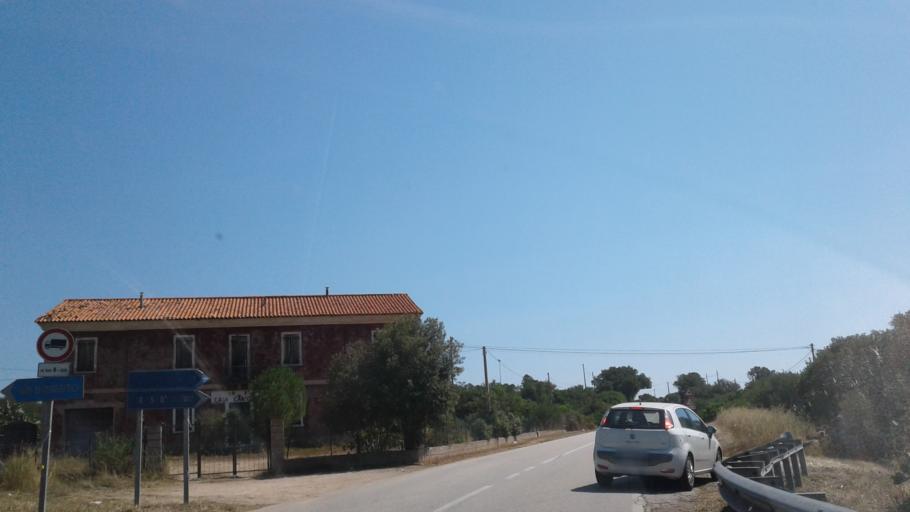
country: IT
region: Sardinia
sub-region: Provincia di Olbia-Tempio
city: Luogosanto
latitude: 41.1155
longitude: 9.2625
